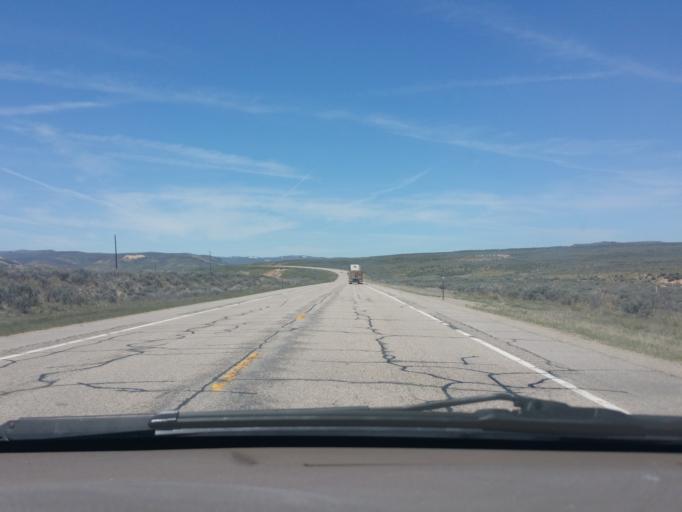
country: US
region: Wyoming
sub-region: Lincoln County
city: Kemmerer
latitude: 41.8157
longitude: -110.6555
